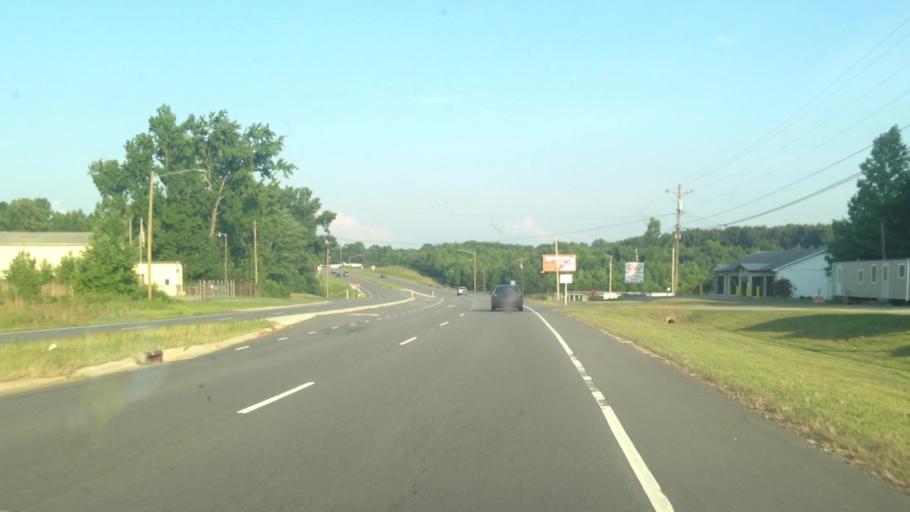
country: US
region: North Carolina
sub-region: Rockingham County
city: Reidsville
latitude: 36.3177
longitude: -79.6806
